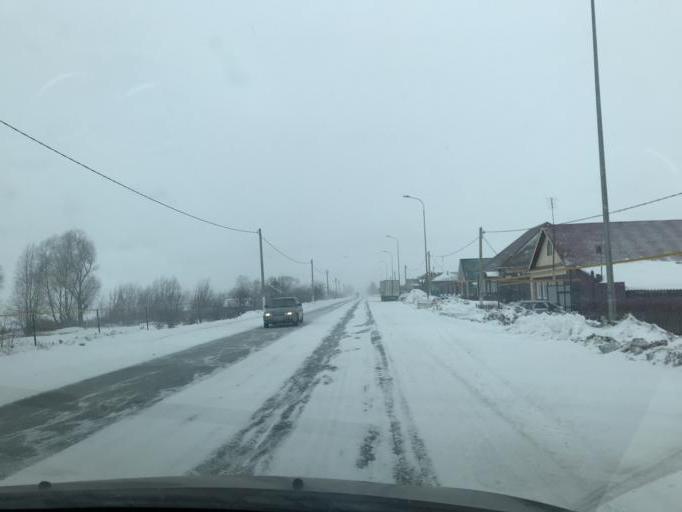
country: RU
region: Tatarstan
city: Buinsk
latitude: 54.9968
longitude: 48.3375
